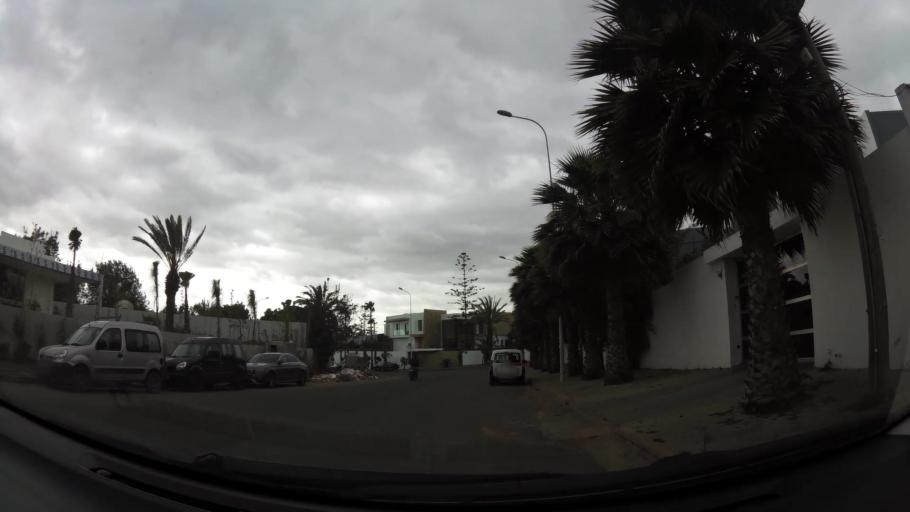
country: MA
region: Grand Casablanca
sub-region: Casablanca
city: Casablanca
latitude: 33.5801
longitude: -7.6704
